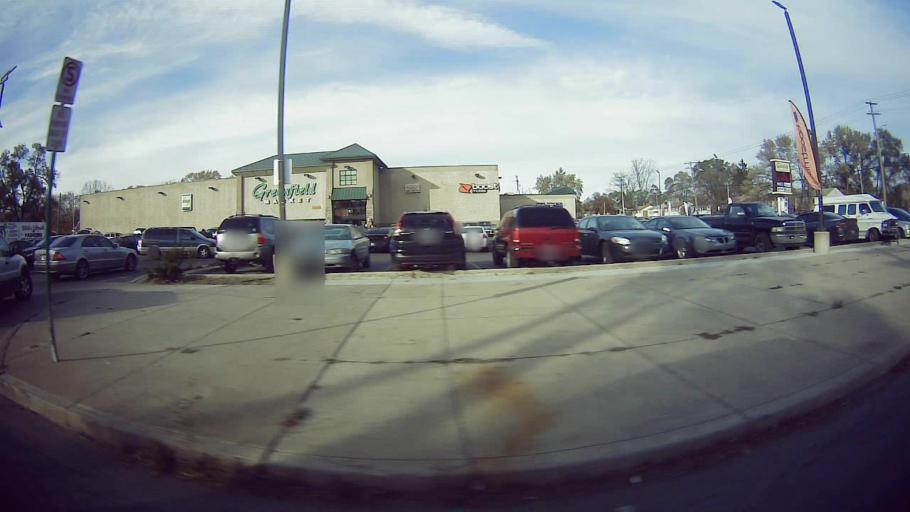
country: US
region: Michigan
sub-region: Oakland County
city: Oak Park
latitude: 42.4088
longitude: -83.1996
